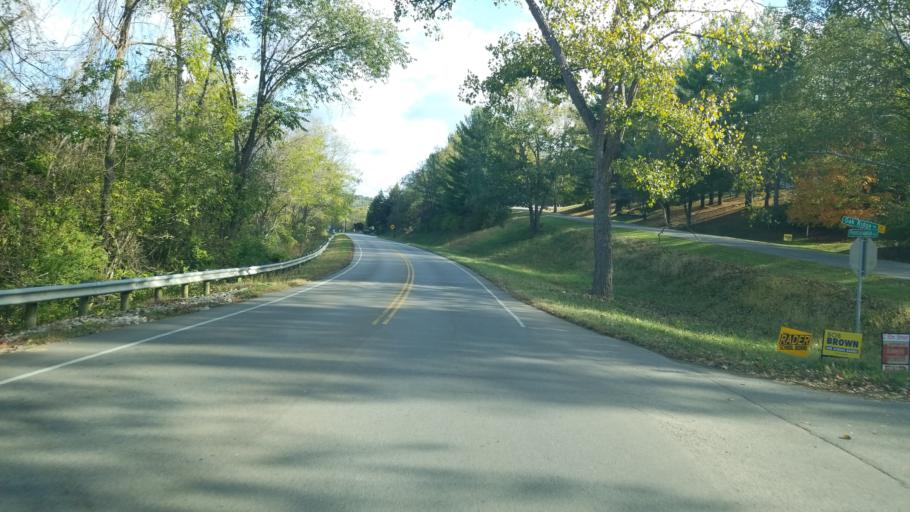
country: US
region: Ohio
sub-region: Jackson County
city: Wellston
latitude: 39.1290
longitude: -82.5320
